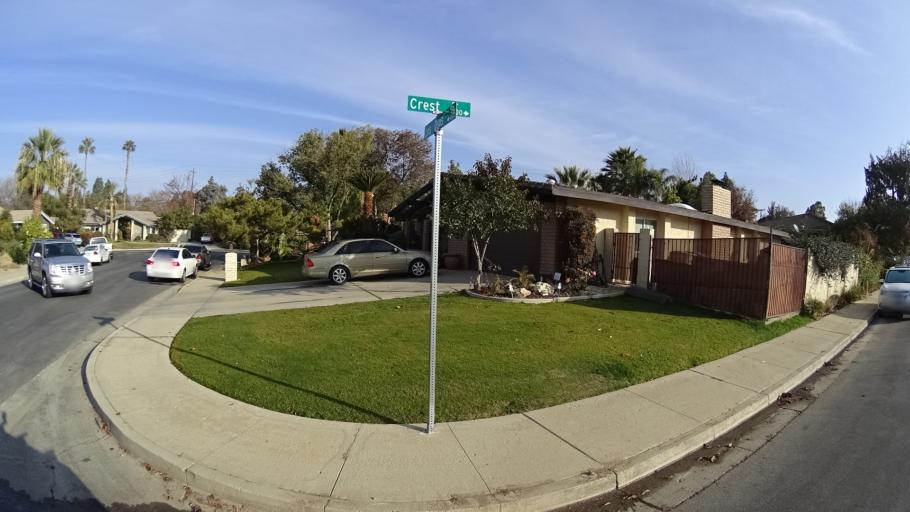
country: US
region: California
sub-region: Kern County
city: Oildale
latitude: 35.4102
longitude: -118.9555
